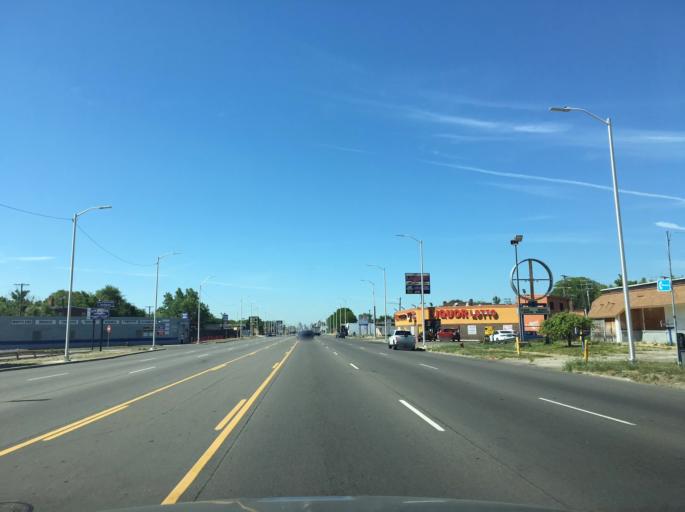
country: US
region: Michigan
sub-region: Wayne County
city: Hamtramck
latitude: 42.4124
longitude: -82.9927
